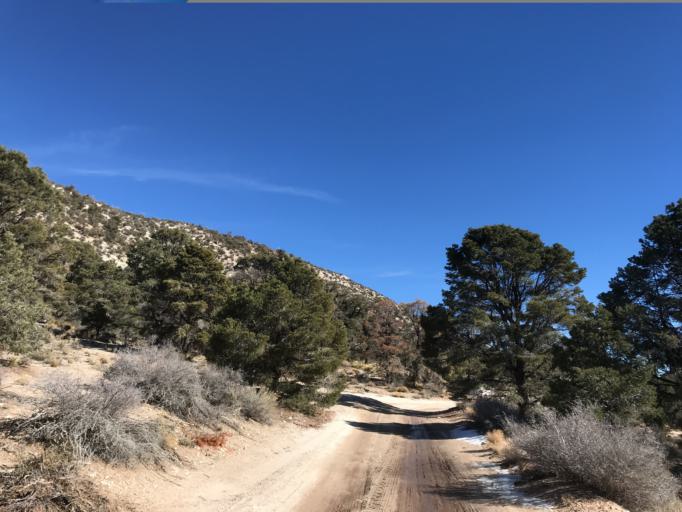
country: US
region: California
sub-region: San Bernardino County
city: Big Bear City
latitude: 34.2415
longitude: -116.6947
